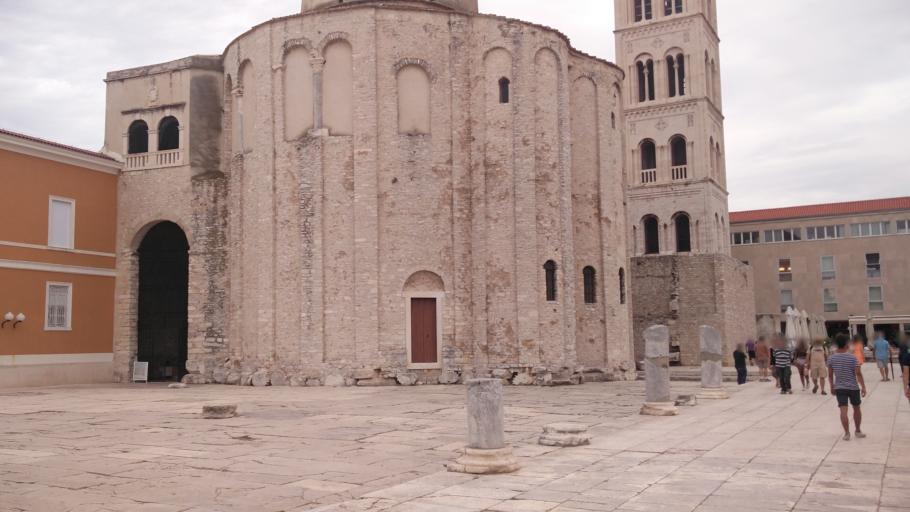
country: HR
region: Zadarska
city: Zadar
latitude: 44.1154
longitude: 15.2243
